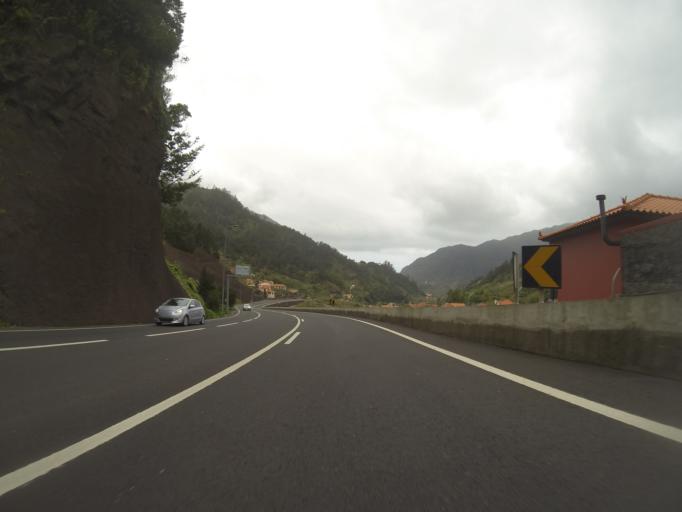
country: PT
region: Madeira
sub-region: Sao Vicente
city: Sao Vicente
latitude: 32.7736
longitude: -17.0305
